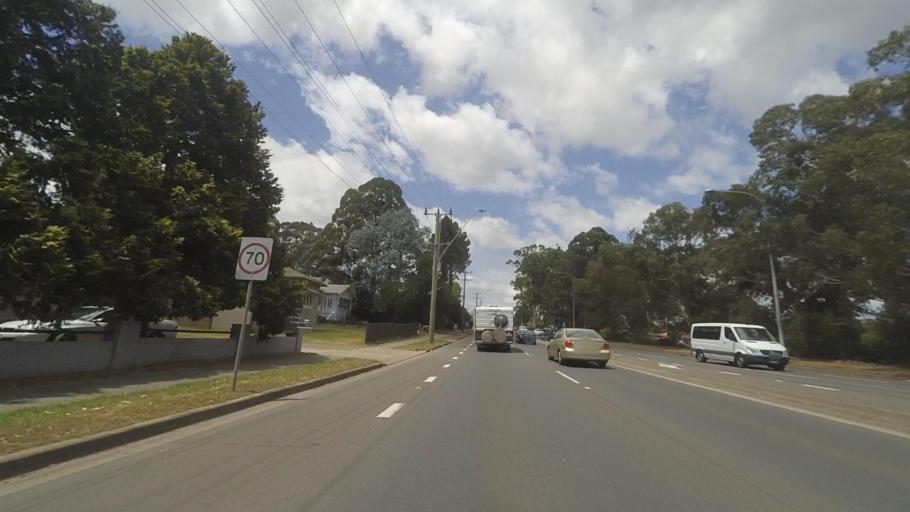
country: AU
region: New South Wales
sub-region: Shoalhaven Shire
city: Nowra
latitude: -34.8794
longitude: 150.6046
